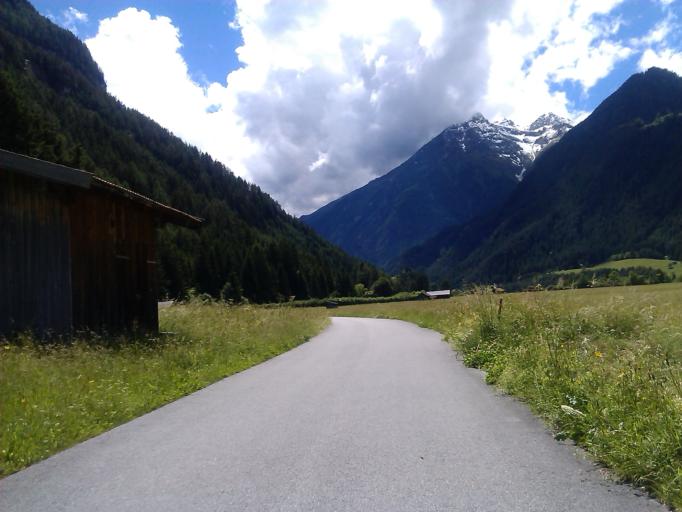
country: AT
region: Tyrol
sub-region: Politischer Bezirk Landeck
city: Pfunds
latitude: 46.9608
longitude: 10.5295
